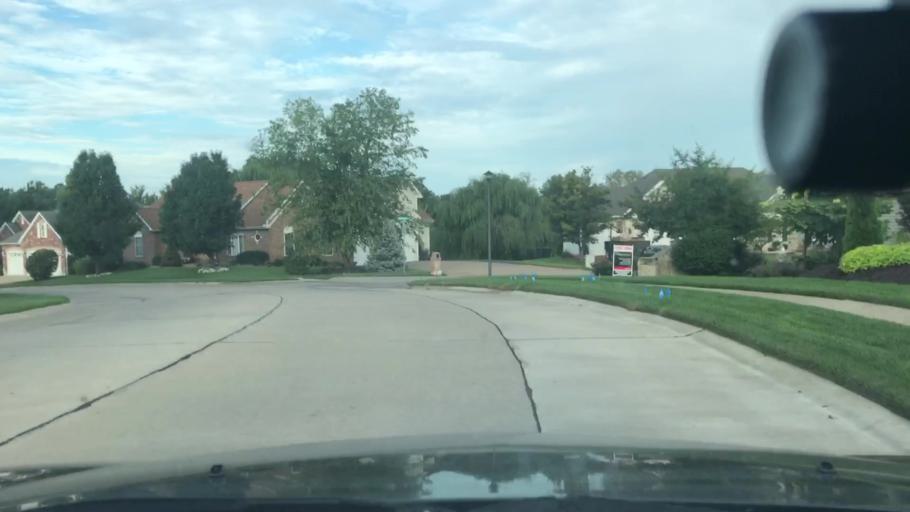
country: US
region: Missouri
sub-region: Saint Charles County
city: Wentzville
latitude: 38.8179
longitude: -90.8991
